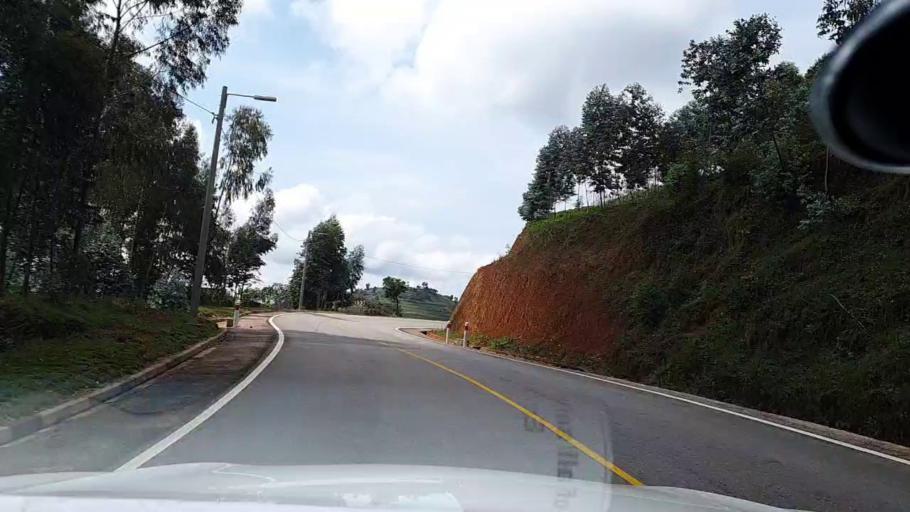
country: RW
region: Southern Province
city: Nzega
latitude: -2.5137
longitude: 29.4632
